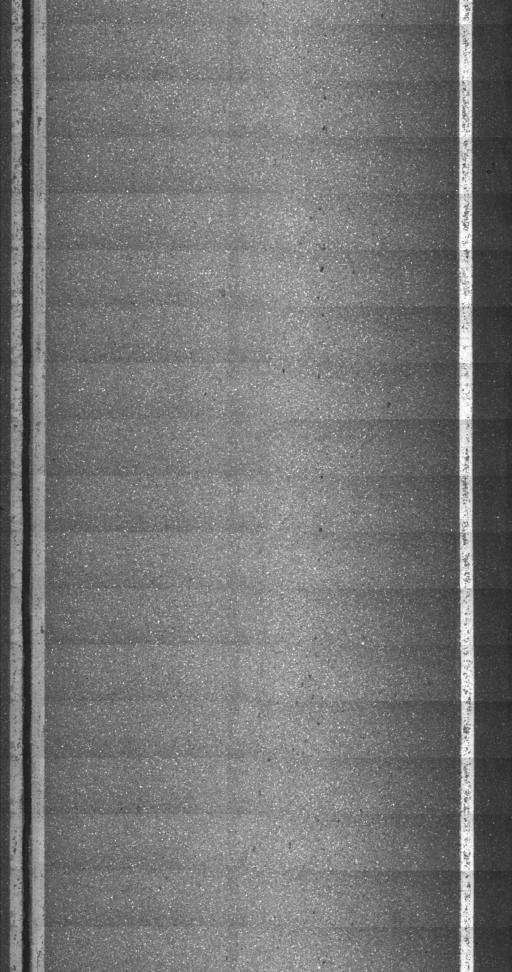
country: US
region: Vermont
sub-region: Orleans County
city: Newport
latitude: 44.9336
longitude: -72.4107
